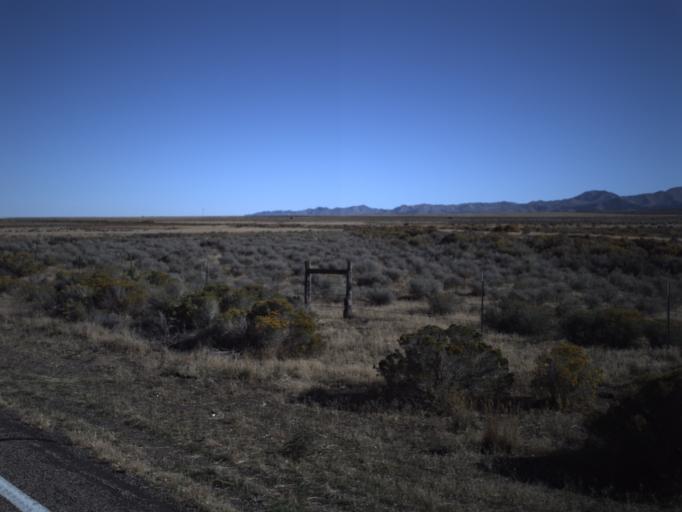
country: US
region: Utah
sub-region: Beaver County
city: Milford
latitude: 38.3248
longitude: -112.9715
